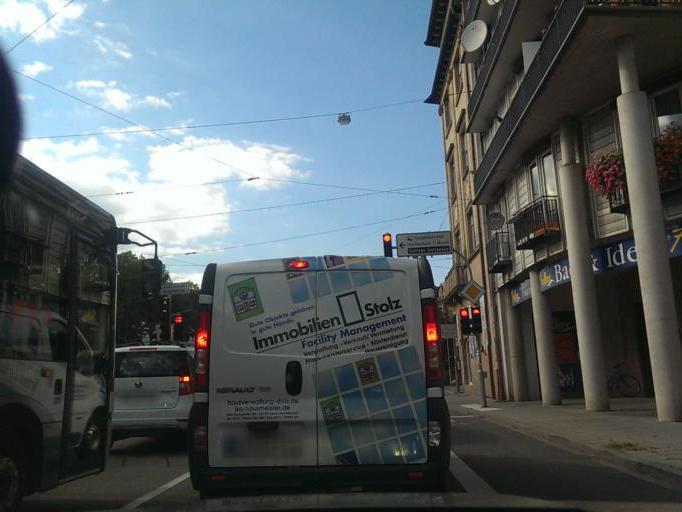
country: DE
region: Baden-Wuerttemberg
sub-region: Karlsruhe Region
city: Karlsruhe
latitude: 49.0076
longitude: 8.4245
